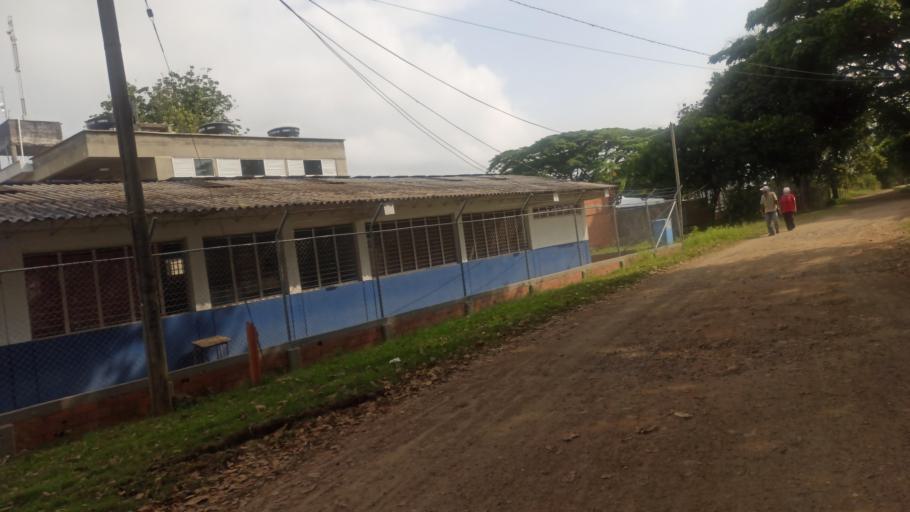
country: CO
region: Valle del Cauca
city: Jamundi
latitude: 3.2014
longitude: -76.5004
